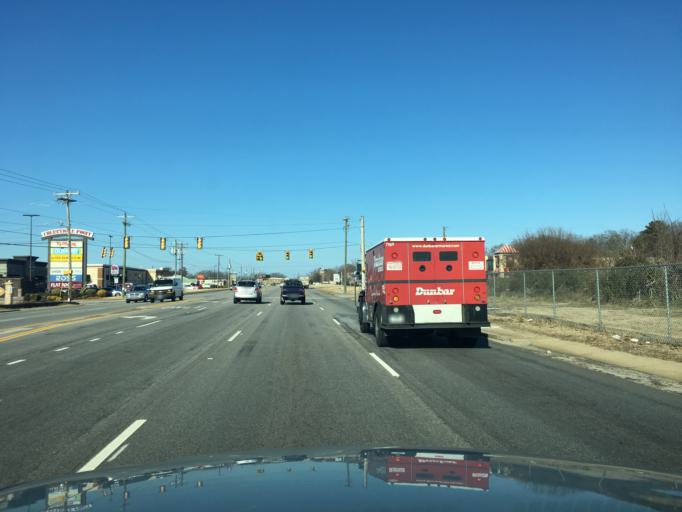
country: US
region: South Carolina
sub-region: Greenville County
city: Sans Souci
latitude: 34.8886
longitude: -82.3981
